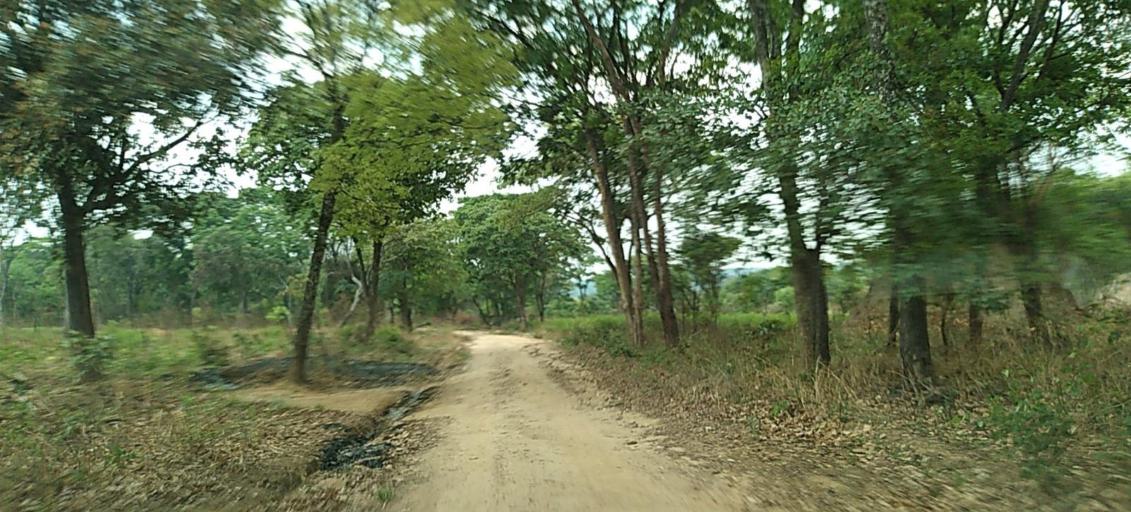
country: ZM
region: Copperbelt
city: Chingola
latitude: -12.7534
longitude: 27.7226
